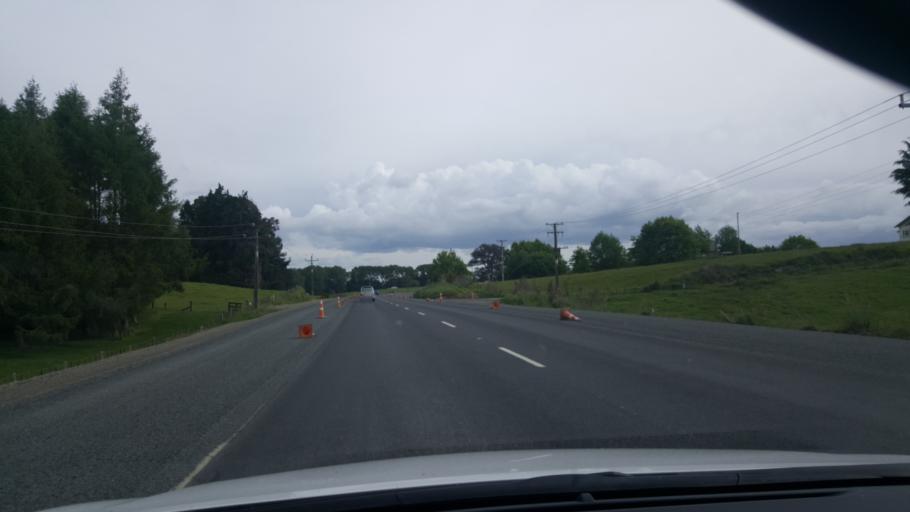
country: NZ
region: Bay of Plenty
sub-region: Rotorua District
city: Rotorua
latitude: -38.4158
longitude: 176.3192
